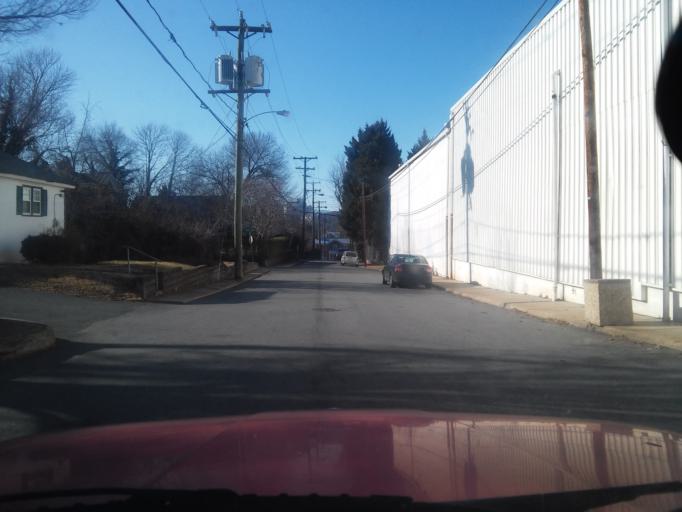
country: US
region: Virginia
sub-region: City of Charlottesville
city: Charlottesville
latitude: 38.0284
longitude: -78.4870
